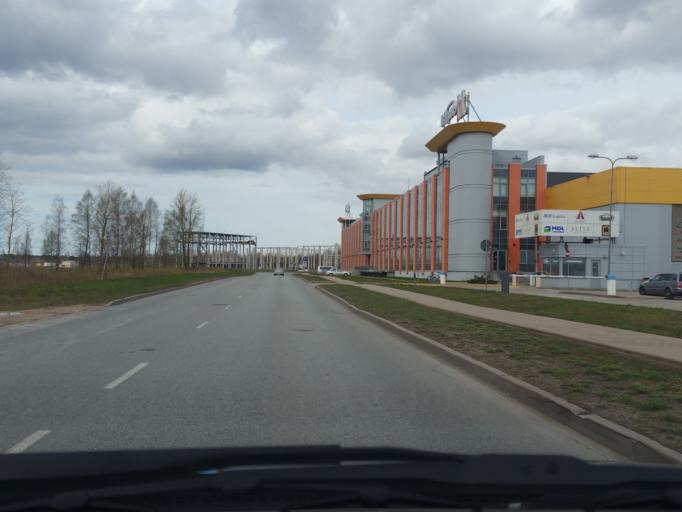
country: LV
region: Marupe
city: Marupe
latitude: 56.9242
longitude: 23.9928
